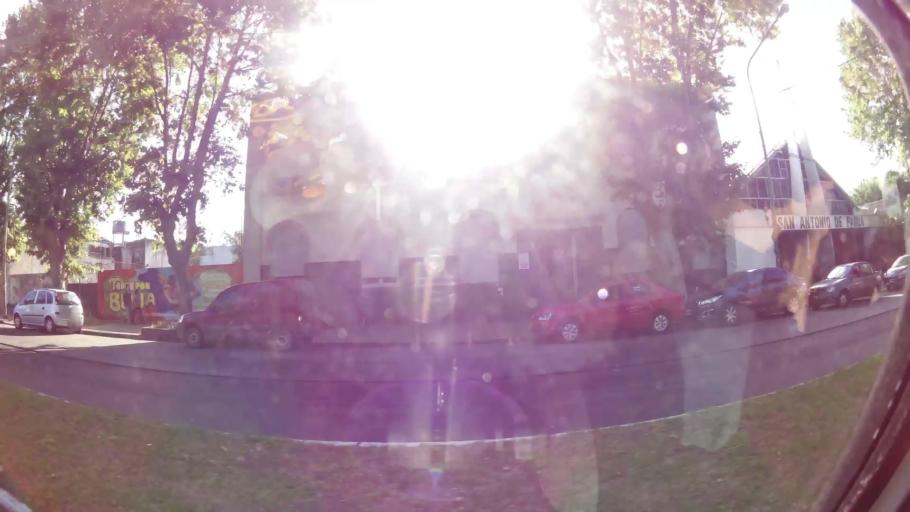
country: AR
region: Buenos Aires
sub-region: Partido de La Plata
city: La Plata
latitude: -34.8973
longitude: -57.9496
